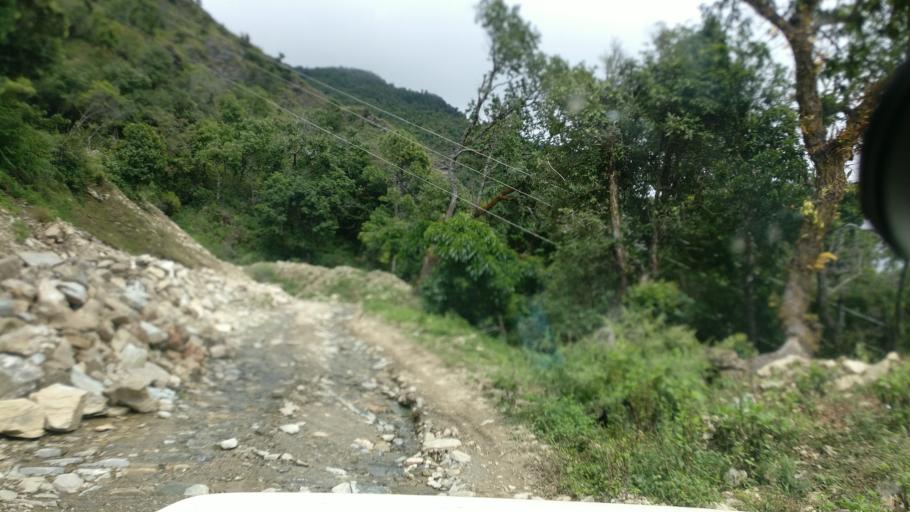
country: NP
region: Western Region
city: Baglung
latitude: 28.2763
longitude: 83.6413
